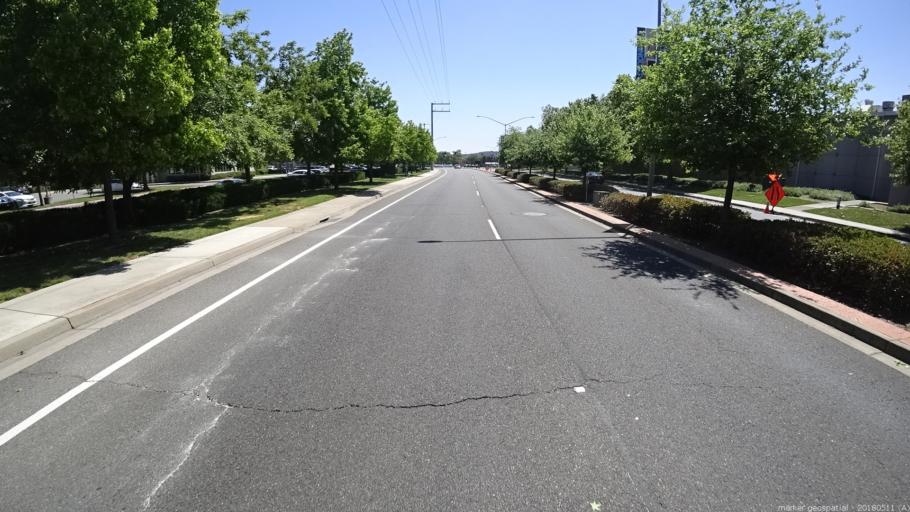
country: US
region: California
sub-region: Sacramento County
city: Sacramento
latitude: 38.6469
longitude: -121.5048
